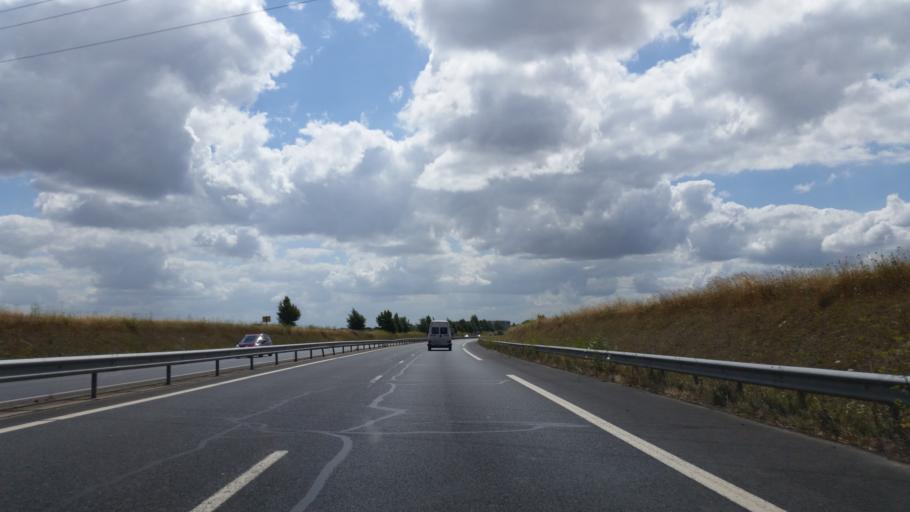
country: FR
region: Lower Normandy
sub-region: Departement du Calvados
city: Falaise
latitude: 48.9202
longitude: -0.2057
